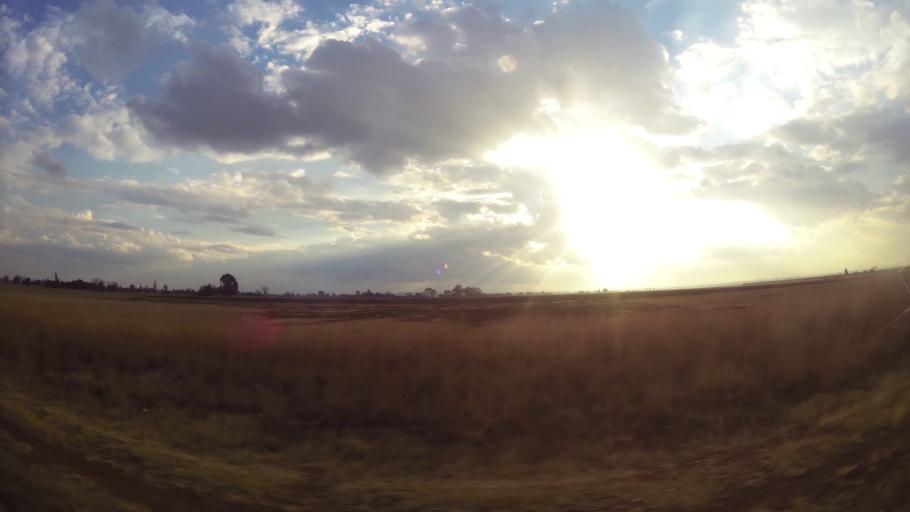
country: ZA
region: Gauteng
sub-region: Sedibeng District Municipality
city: Vanderbijlpark
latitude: -26.6268
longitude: 27.8101
